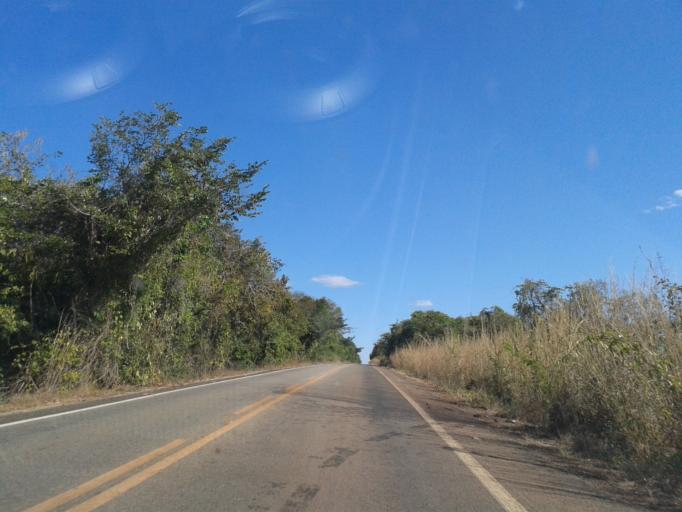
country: BR
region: Goias
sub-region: Mozarlandia
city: Mozarlandia
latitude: -14.4330
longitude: -50.4555
